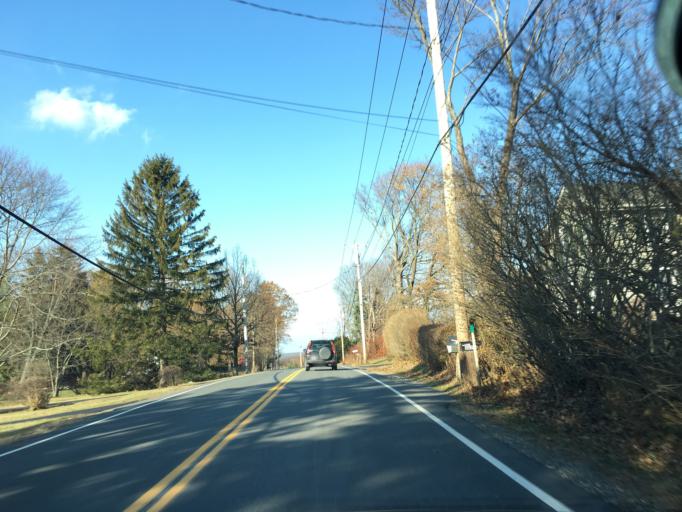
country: US
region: New York
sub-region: Rensselaer County
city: Hampton Manor
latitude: 42.6486
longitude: -73.6880
